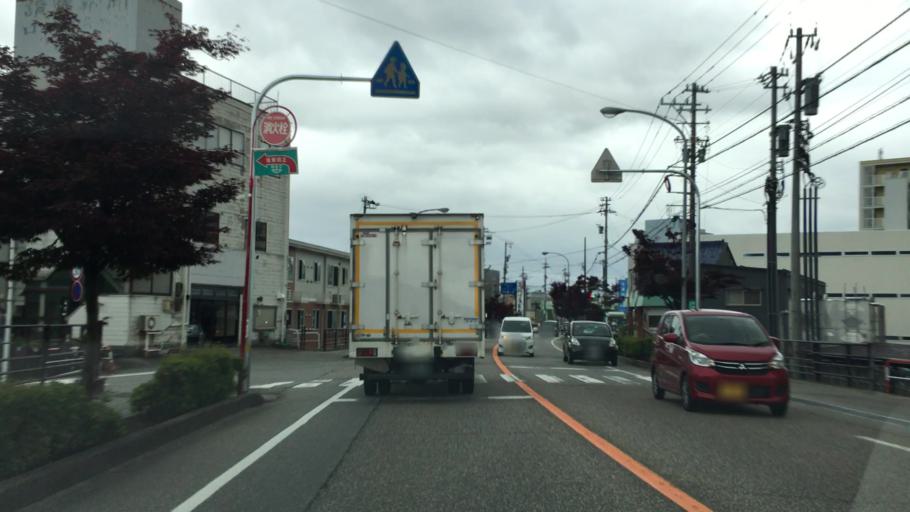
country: JP
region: Toyama
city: Toyama-shi
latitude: 36.7029
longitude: 137.1866
